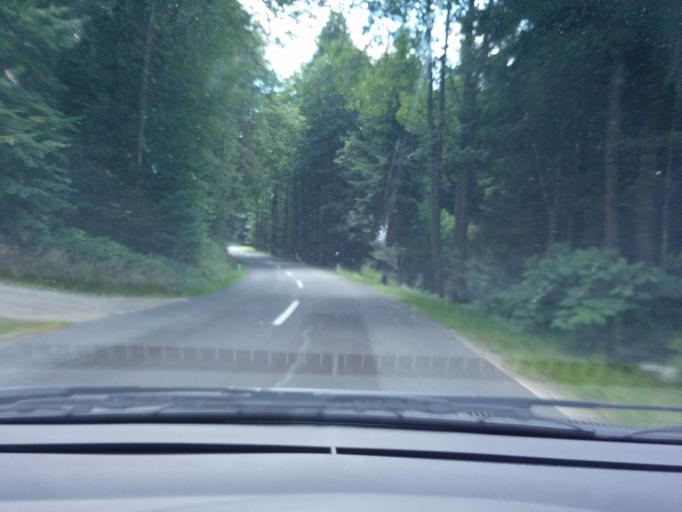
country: AT
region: Upper Austria
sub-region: Politischer Bezirk Rohrbach
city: Ulrichsberg
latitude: 48.7190
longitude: 13.8978
